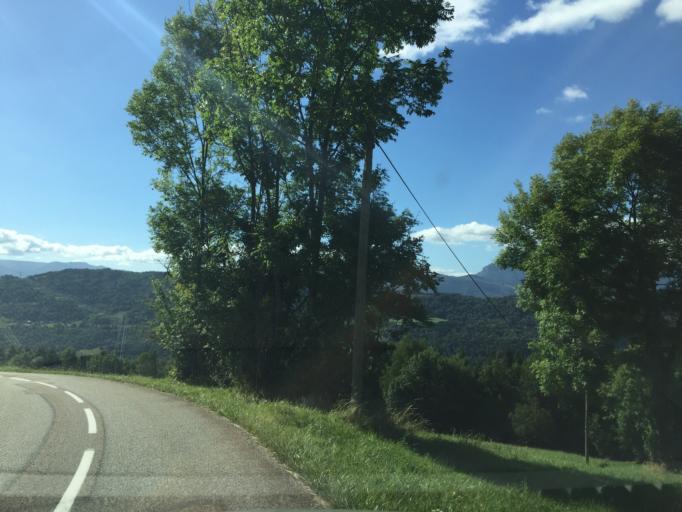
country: FR
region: Rhone-Alpes
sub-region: Departement de la Savoie
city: La Rochette
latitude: 45.4776
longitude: 6.1603
